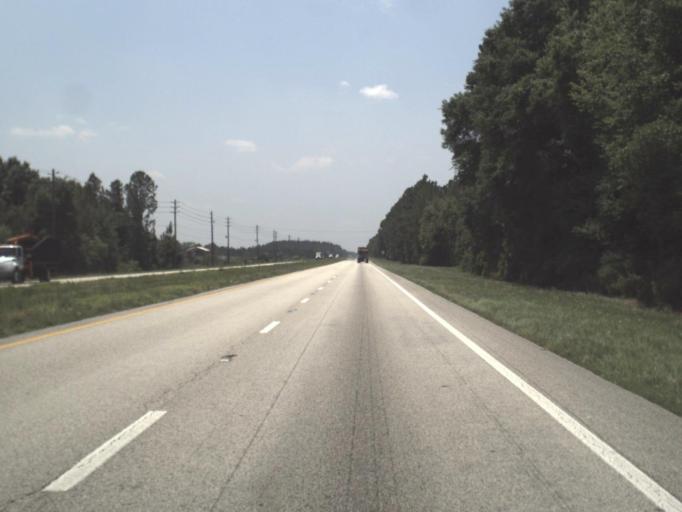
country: US
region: Florida
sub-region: Duval County
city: Baldwin
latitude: 30.2473
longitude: -81.9972
